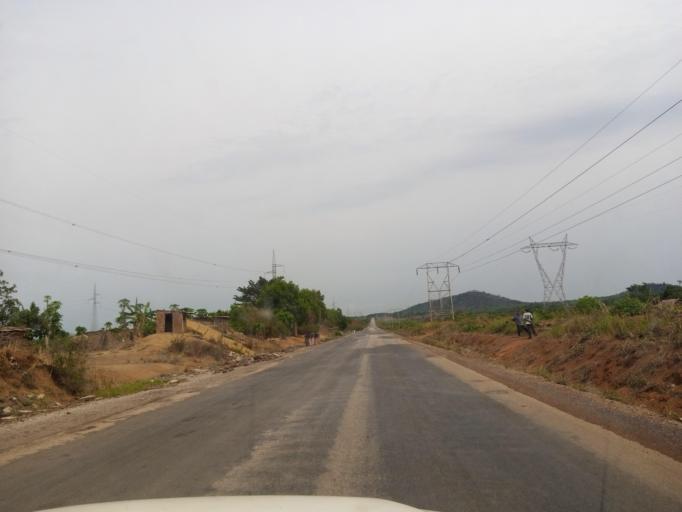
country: CD
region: Katanga
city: Likasi
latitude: -11.0878
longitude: 27.0013
